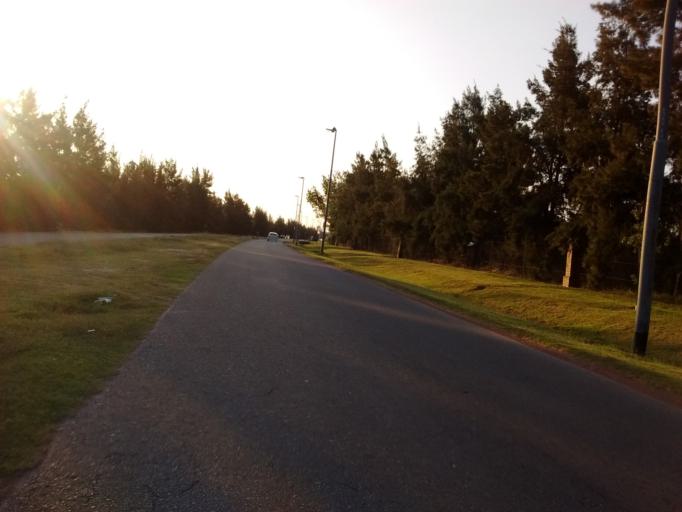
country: AR
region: Santa Fe
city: Funes
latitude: -32.9194
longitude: -60.7702
